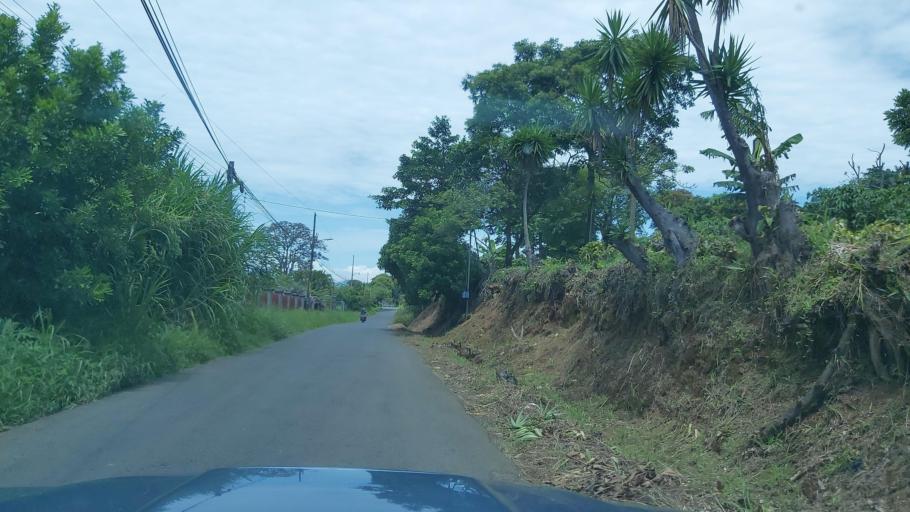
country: CR
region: Alajuela
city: San Juan
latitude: 10.1016
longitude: -84.3353
